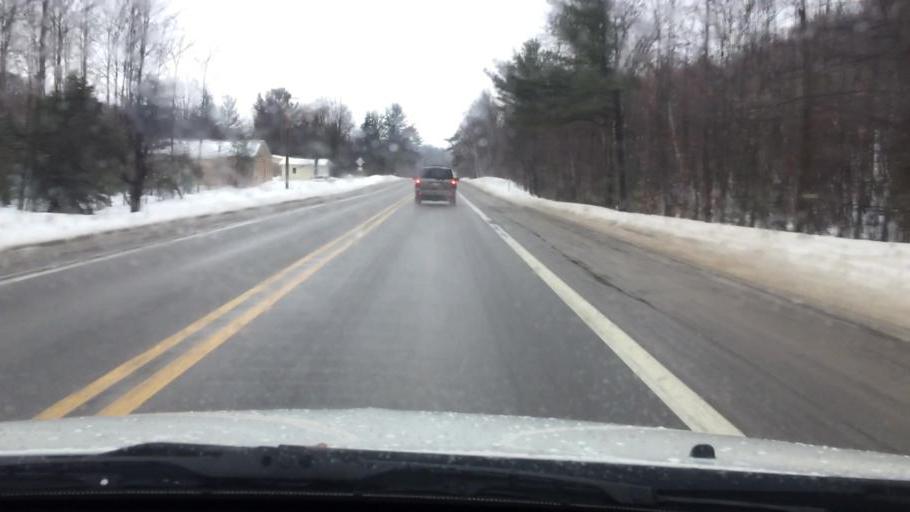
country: US
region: Michigan
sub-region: Charlevoix County
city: East Jordan
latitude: 45.2271
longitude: -85.1808
